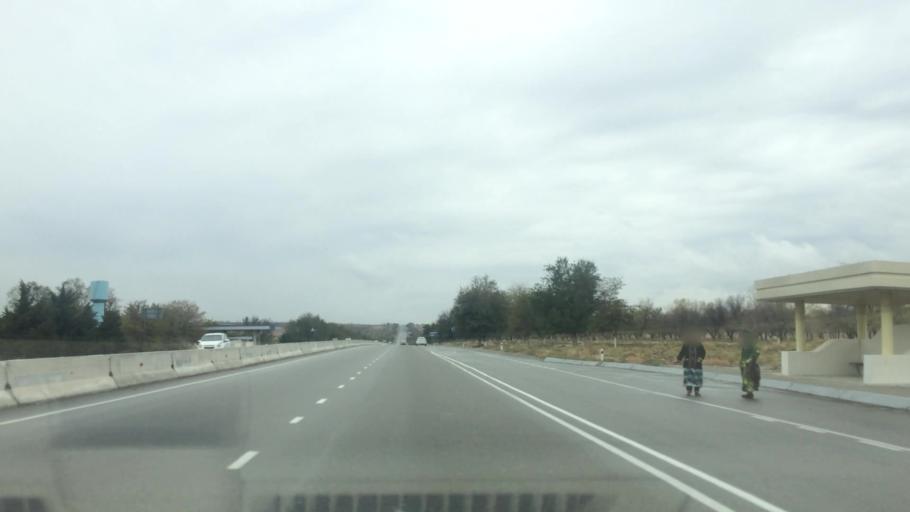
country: UZ
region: Samarqand
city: Bulung'ur
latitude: 39.8817
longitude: 67.4865
